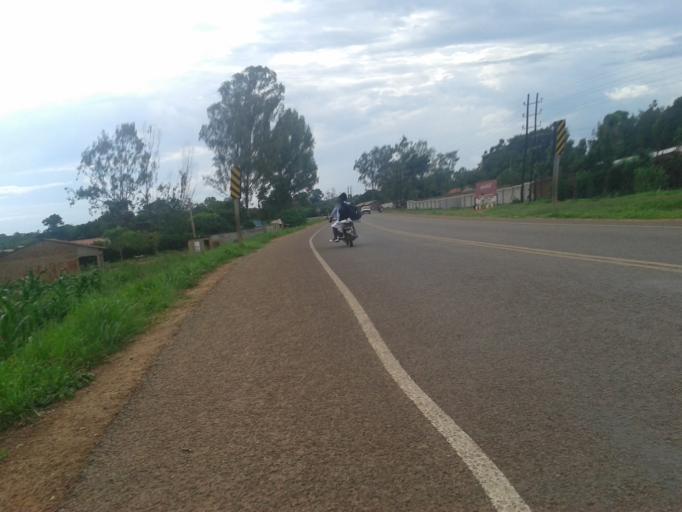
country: UG
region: Northern Region
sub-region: Gulu District
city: Gulu
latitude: 2.7626
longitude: 32.2731
